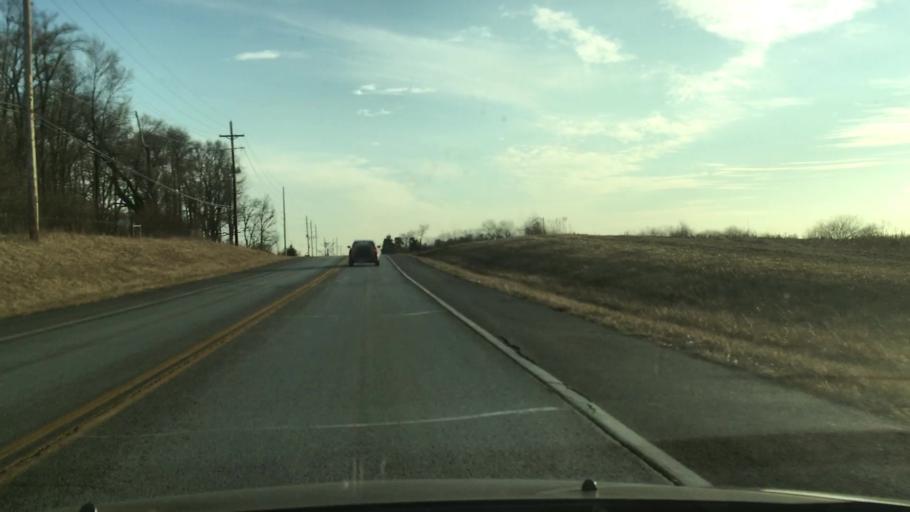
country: US
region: Missouri
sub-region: Jackson County
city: Lees Summit
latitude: 38.8851
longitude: -94.4152
